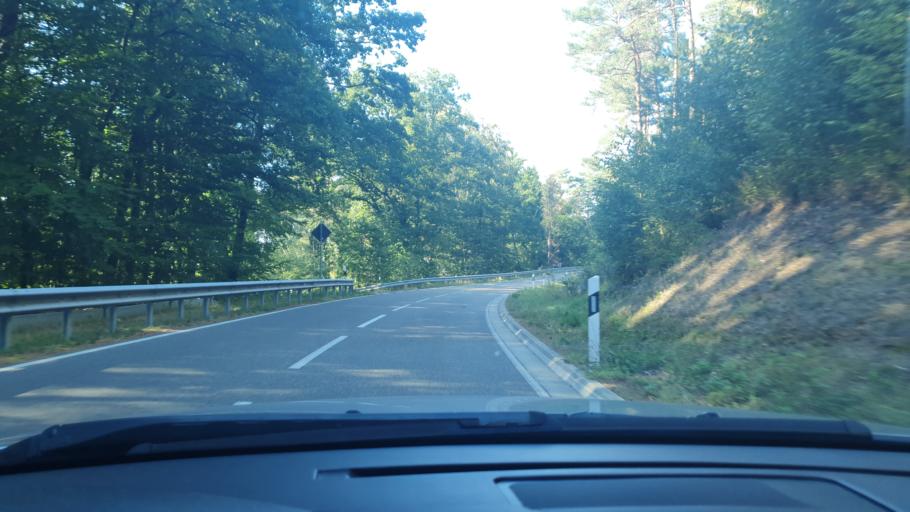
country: DE
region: Rheinland-Pfalz
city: Heltersberg
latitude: 49.3283
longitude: 7.7184
